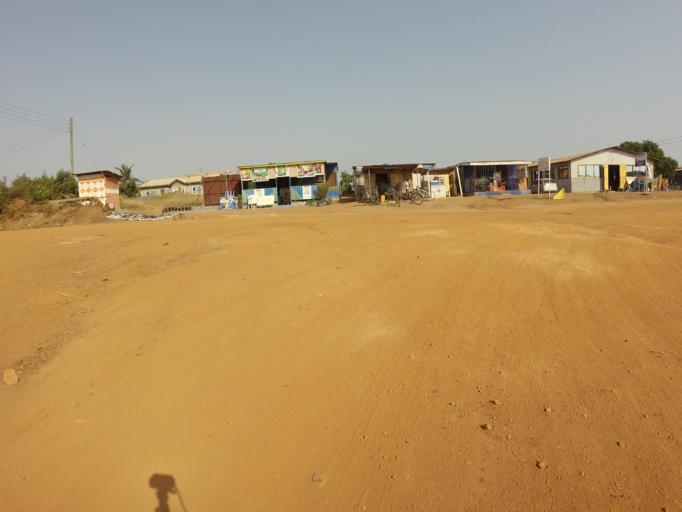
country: GH
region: Greater Accra
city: Tema
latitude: 5.7056
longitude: 0.0590
